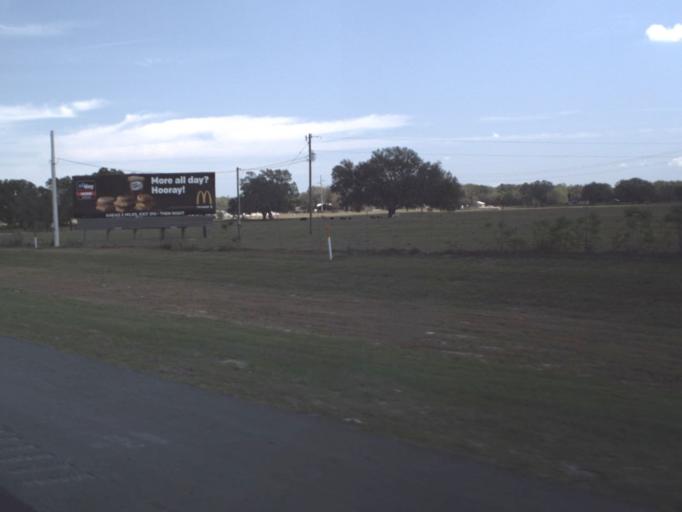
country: US
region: Florida
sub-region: Sumter County
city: Bushnell
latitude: 28.6399
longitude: -82.1623
